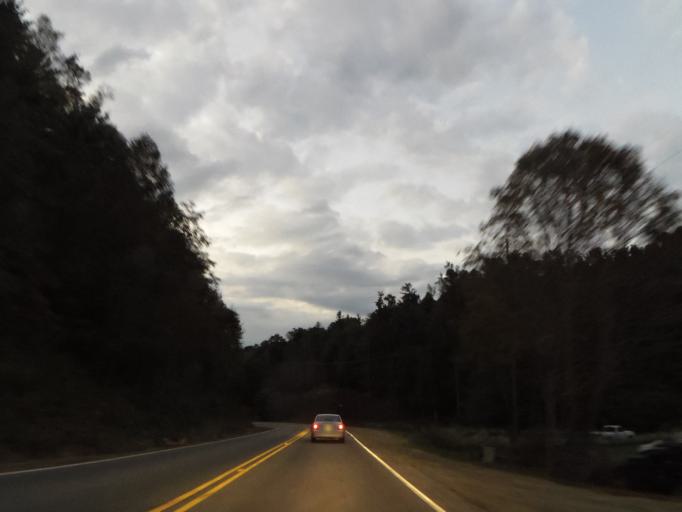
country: US
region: North Carolina
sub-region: Madison County
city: Marshall
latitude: 35.8467
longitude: -82.7306
